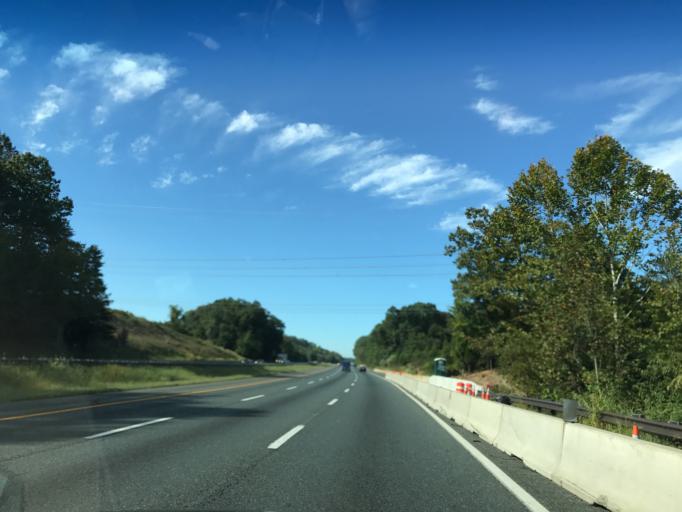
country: US
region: Maryland
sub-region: Anne Arundel County
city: Riva
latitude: 38.9751
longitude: -76.6176
